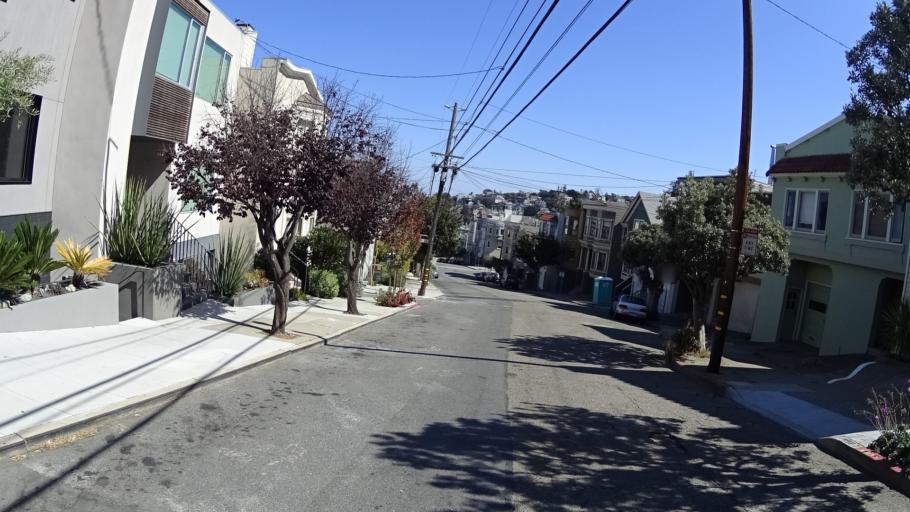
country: US
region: California
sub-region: San Francisco County
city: San Francisco
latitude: 37.7591
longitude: -122.4404
